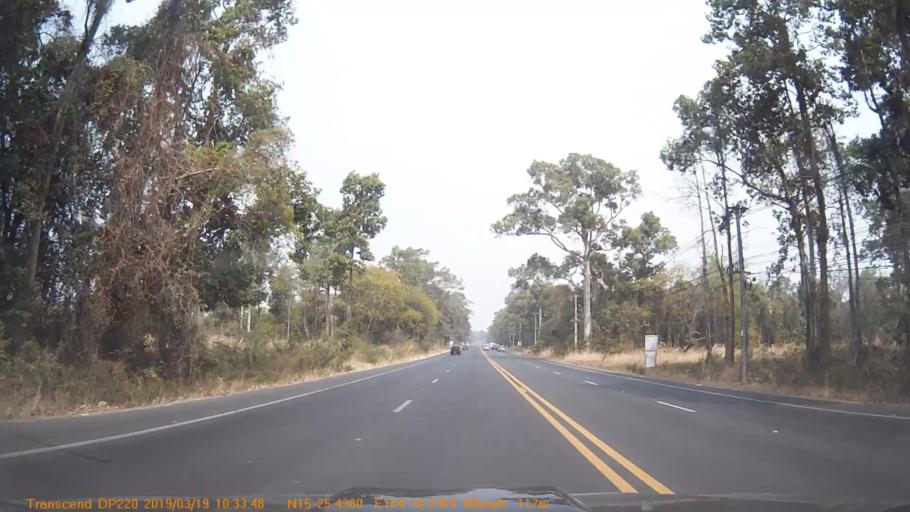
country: TH
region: Changwat Ubon Ratchathani
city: Khueang Nai
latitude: 15.4243
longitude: 104.5373
